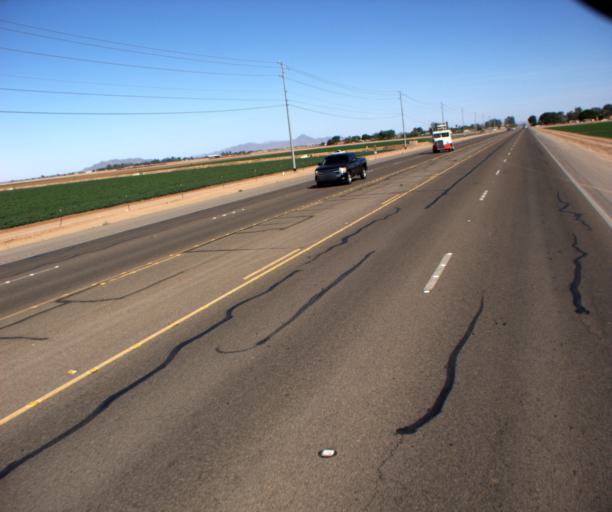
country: US
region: Arizona
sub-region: Yuma County
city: Somerton
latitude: 32.6278
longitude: -114.6498
